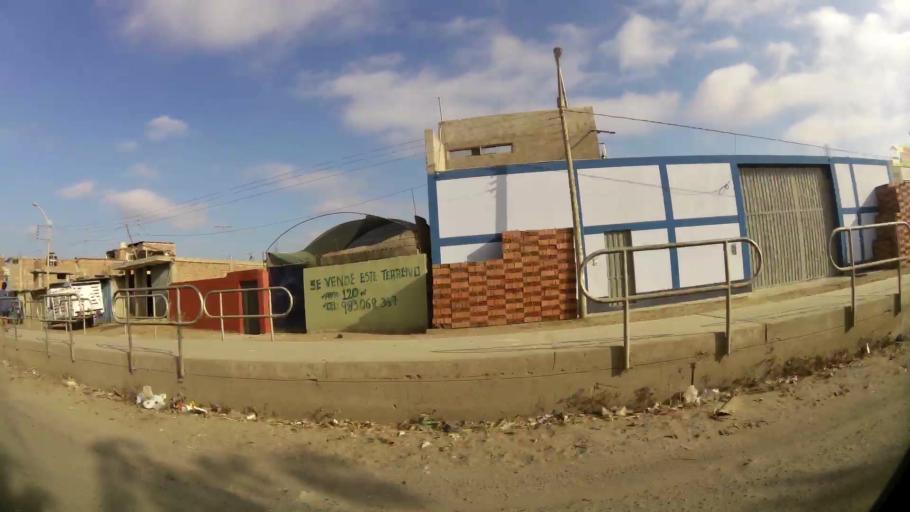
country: PE
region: La Libertad
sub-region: Provincia de Trujillo
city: La Esperanza
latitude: -8.0870
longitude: -79.0381
